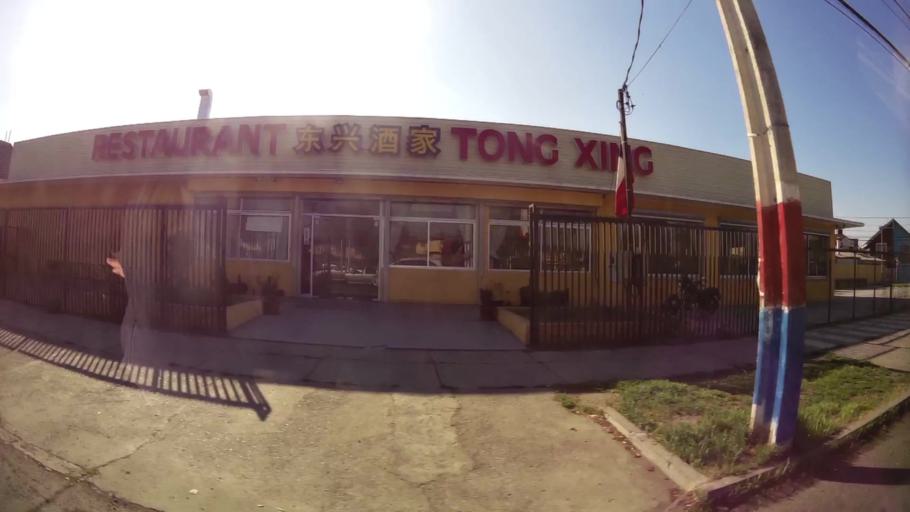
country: CL
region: Santiago Metropolitan
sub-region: Provincia de Santiago
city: Lo Prado
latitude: -33.4876
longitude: -70.7718
